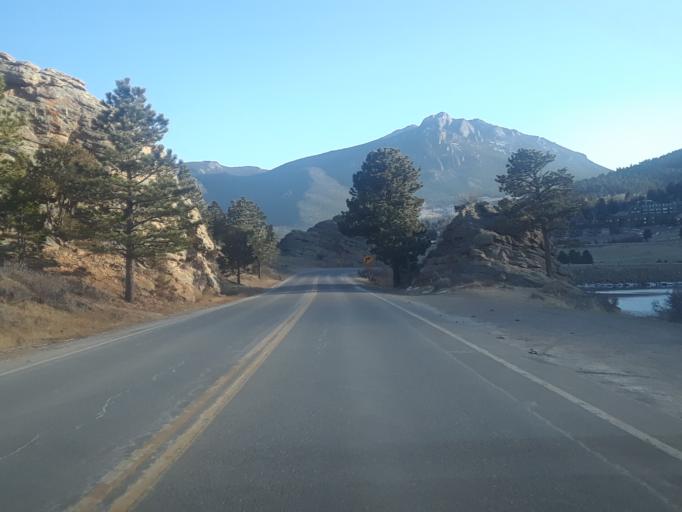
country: US
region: Colorado
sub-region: Larimer County
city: Estes Park
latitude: 40.3443
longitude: -105.5299
